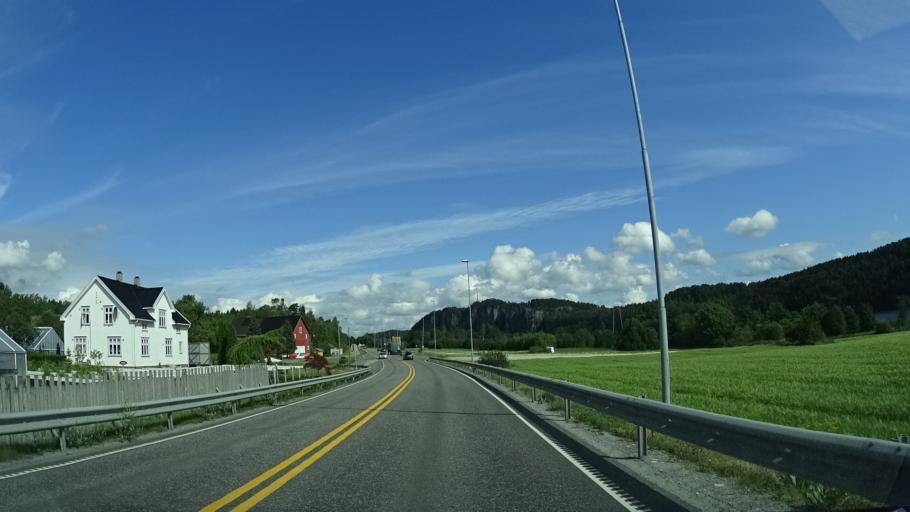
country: NO
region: Telemark
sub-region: Bamble
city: Langesund
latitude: 59.0283
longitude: 9.6802
